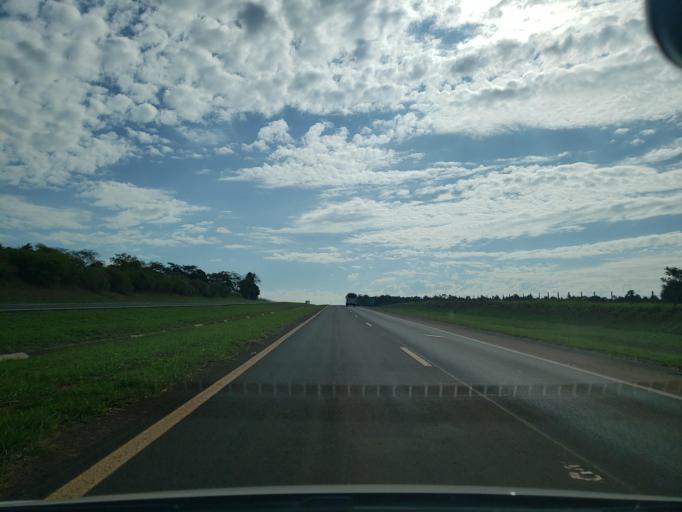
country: BR
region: Sao Paulo
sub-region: Promissao
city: Promissao
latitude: -21.6087
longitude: -49.8723
